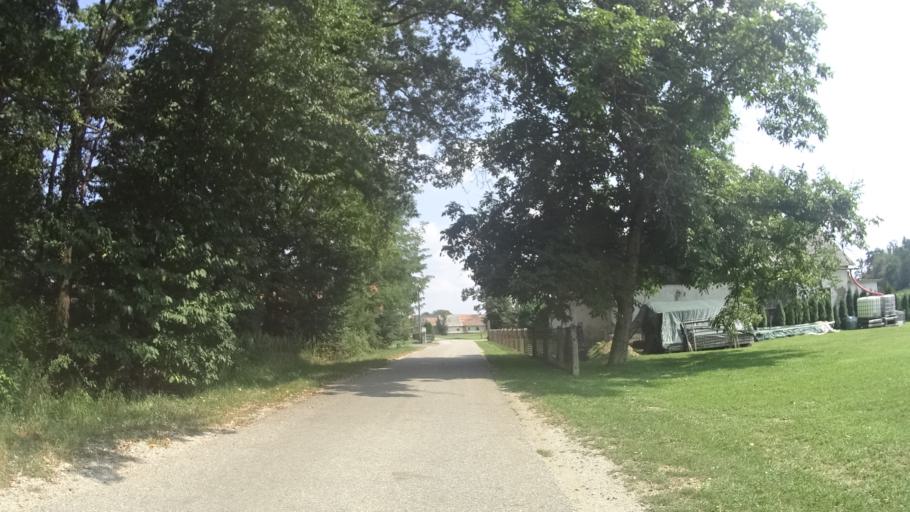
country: SI
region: Starse
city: Starse
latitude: 46.4458
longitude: 15.7514
